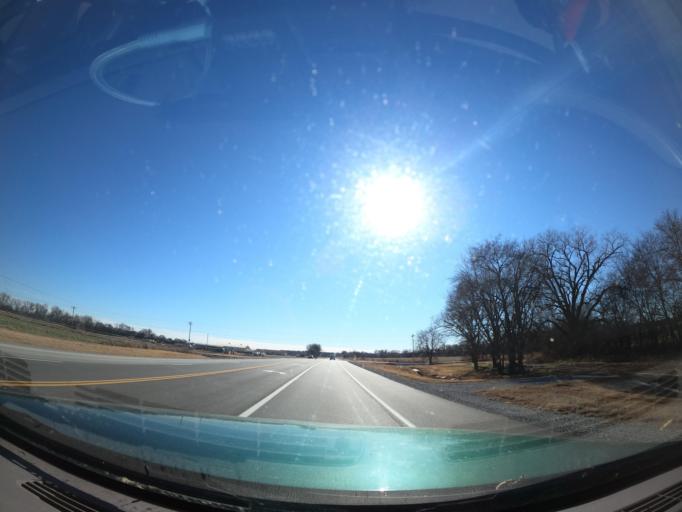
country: US
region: Oklahoma
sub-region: Wagoner County
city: Coweta
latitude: 35.8866
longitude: -95.6593
